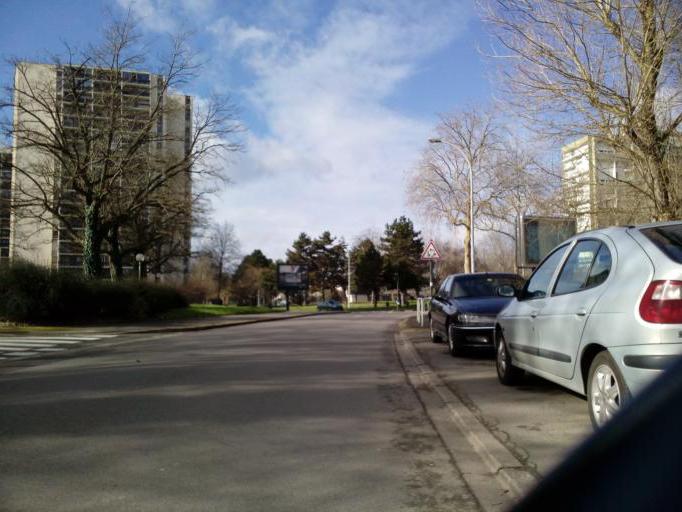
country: FR
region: Brittany
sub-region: Departement d'Ille-et-Vilaine
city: Rennes
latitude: 48.0891
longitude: -1.6811
